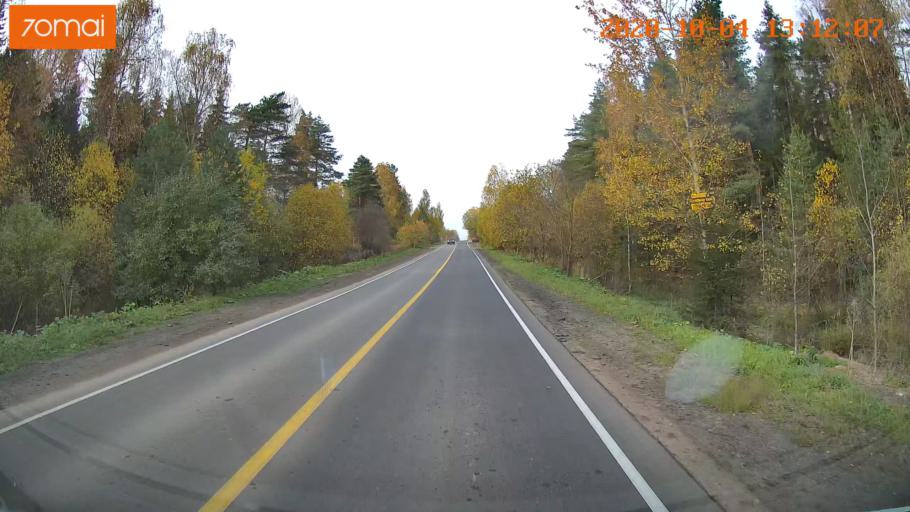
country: RU
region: Ivanovo
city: Bogorodskoye
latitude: 57.0817
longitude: 40.9318
